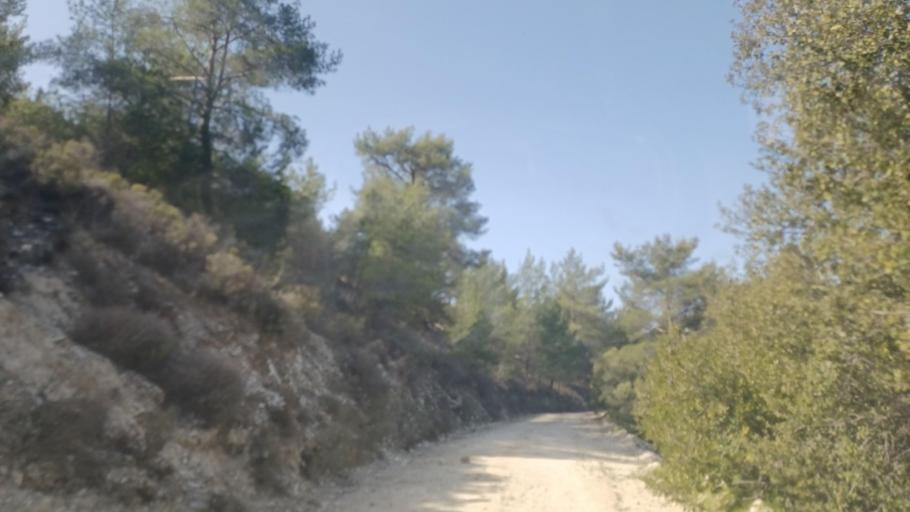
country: CY
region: Limassol
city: Pachna
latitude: 34.8867
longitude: 32.7251
